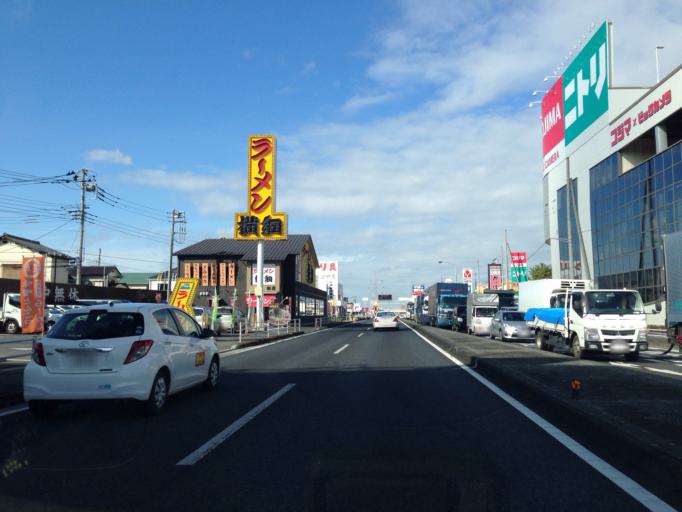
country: JP
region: Chiba
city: Kashiwa
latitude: 35.8795
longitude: 139.9668
